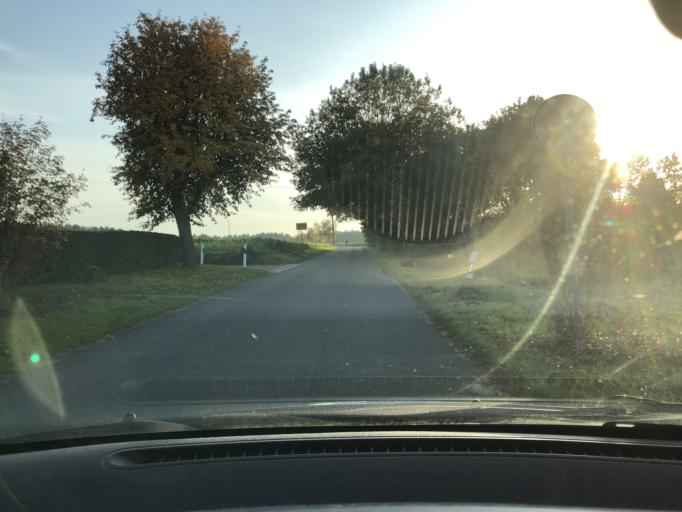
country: DE
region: Lower Saxony
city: Hitzacker
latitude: 53.1367
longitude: 11.0318
